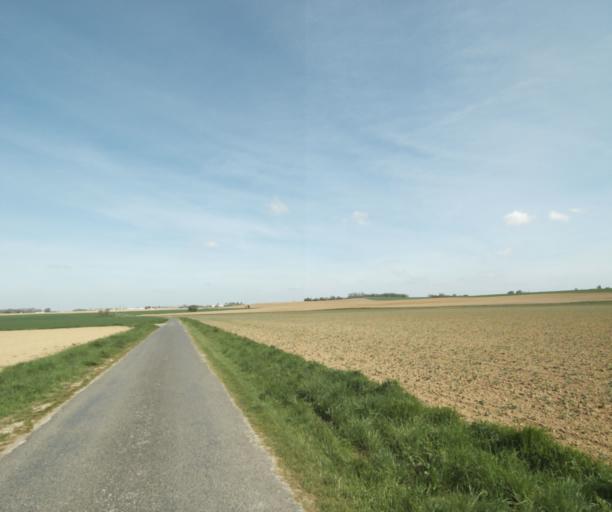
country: FR
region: Ile-de-France
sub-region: Departement de Seine-et-Marne
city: Nangis
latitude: 48.5428
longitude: 3.0368
